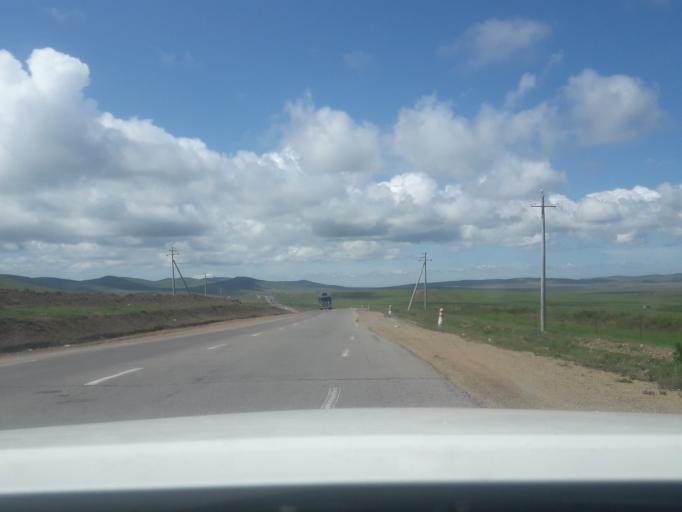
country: MN
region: Central Aimak
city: Altanbulag
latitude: 47.9012
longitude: 106.4965
